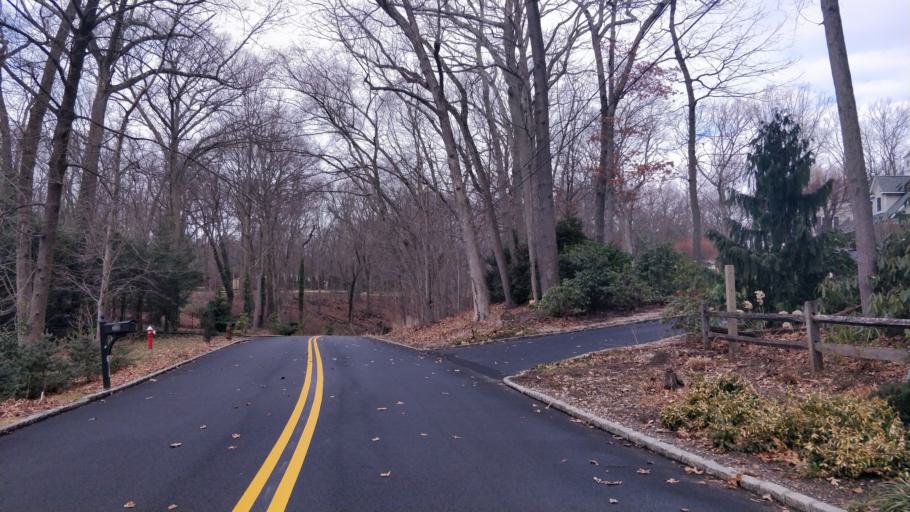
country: US
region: New York
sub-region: Nassau County
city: Laurel Hollow
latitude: 40.8565
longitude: -73.4821
